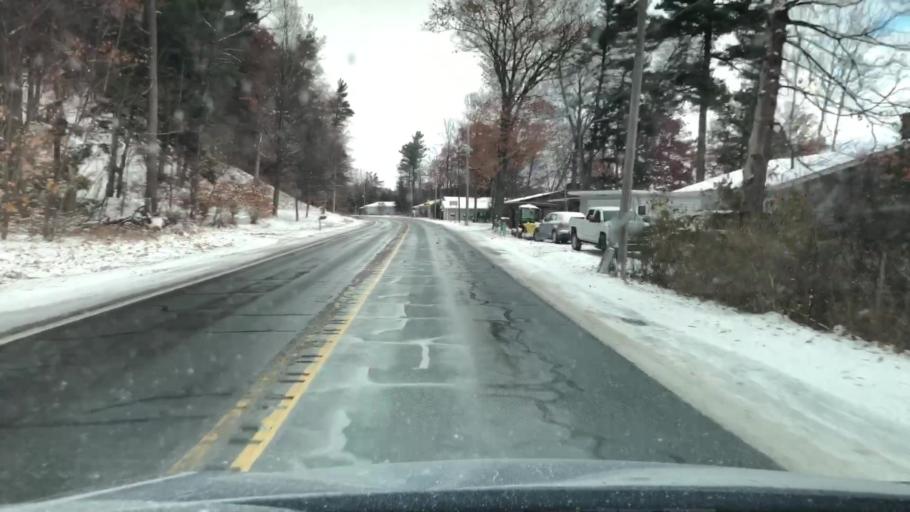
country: US
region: Michigan
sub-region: Grand Traverse County
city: Traverse City
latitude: 44.8300
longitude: -85.5446
